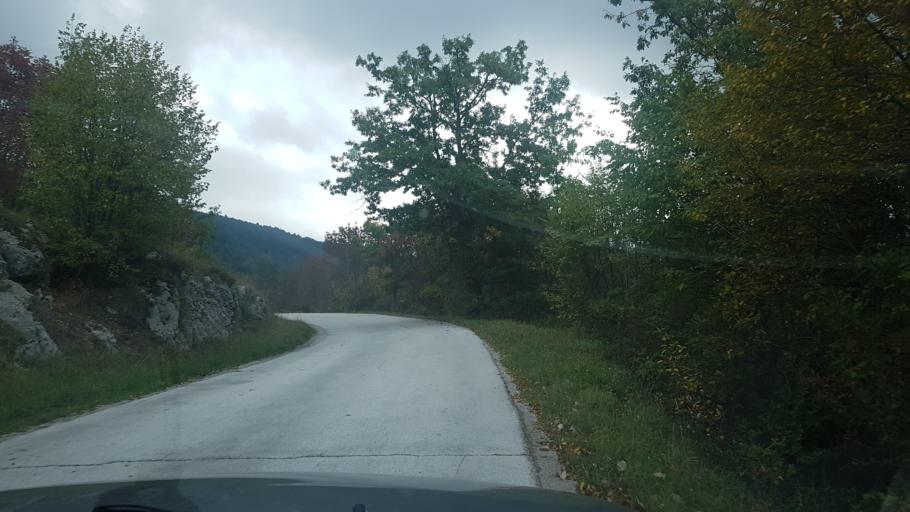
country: HR
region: Istarska
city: Buzet
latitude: 45.5037
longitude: 13.9876
